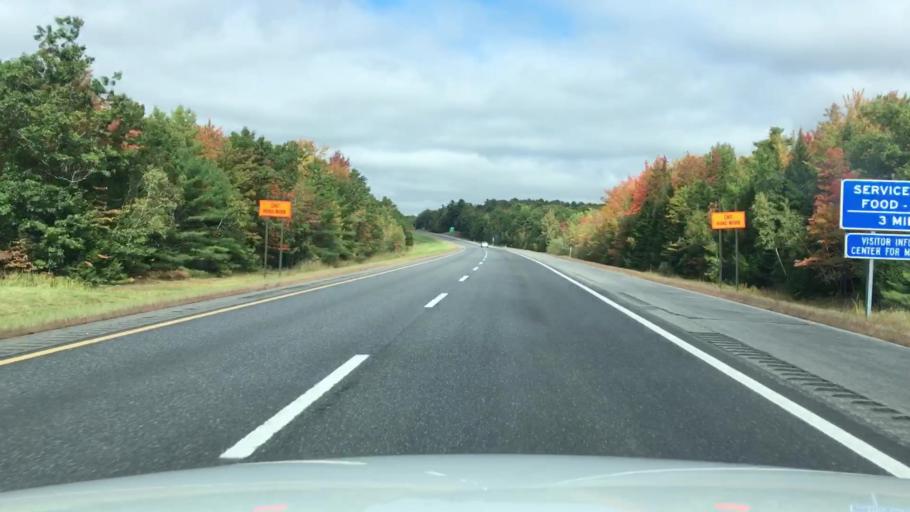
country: US
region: Maine
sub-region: Sagadahoc County
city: Richmond
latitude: 44.1568
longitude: -69.8360
